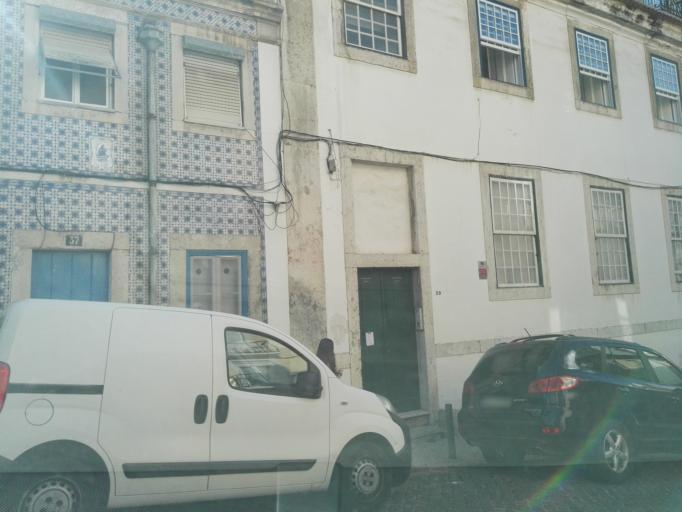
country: PT
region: Setubal
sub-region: Almada
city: Cacilhas
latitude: 38.7073
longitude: -9.1580
